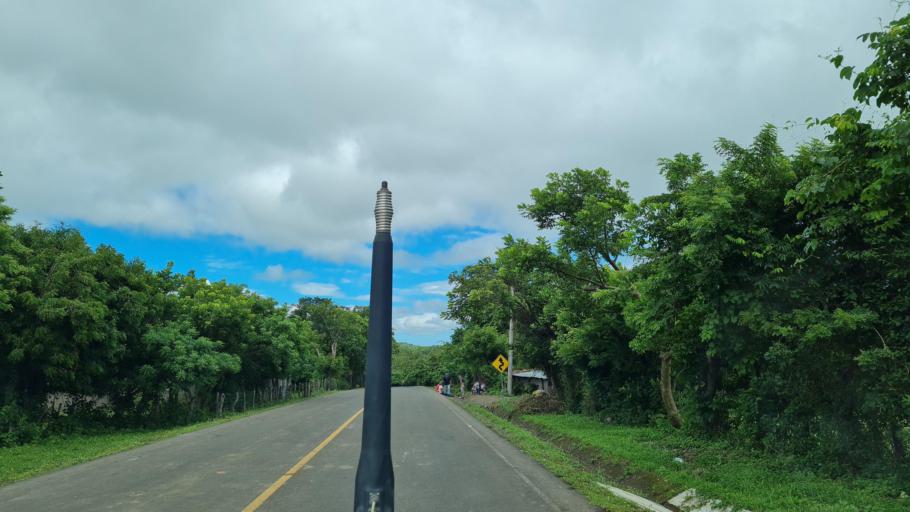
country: NI
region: Matagalpa
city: Terrabona
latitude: 12.5853
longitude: -85.9712
